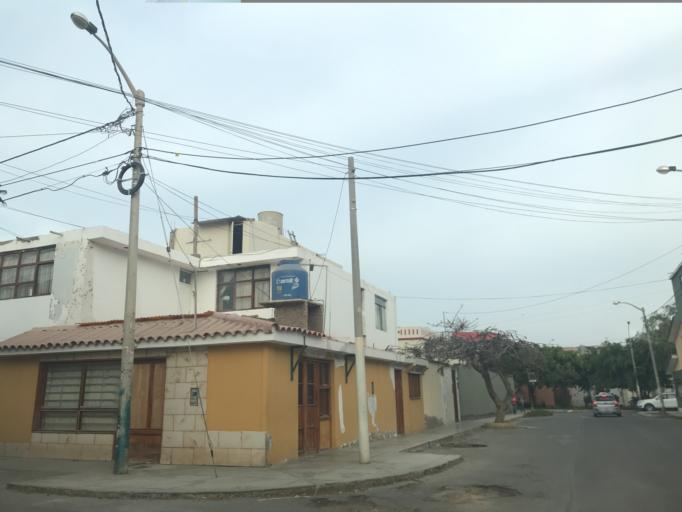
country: PE
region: Lambayeque
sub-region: Provincia de Chiclayo
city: Chiclayo
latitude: -6.7865
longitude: -79.8435
